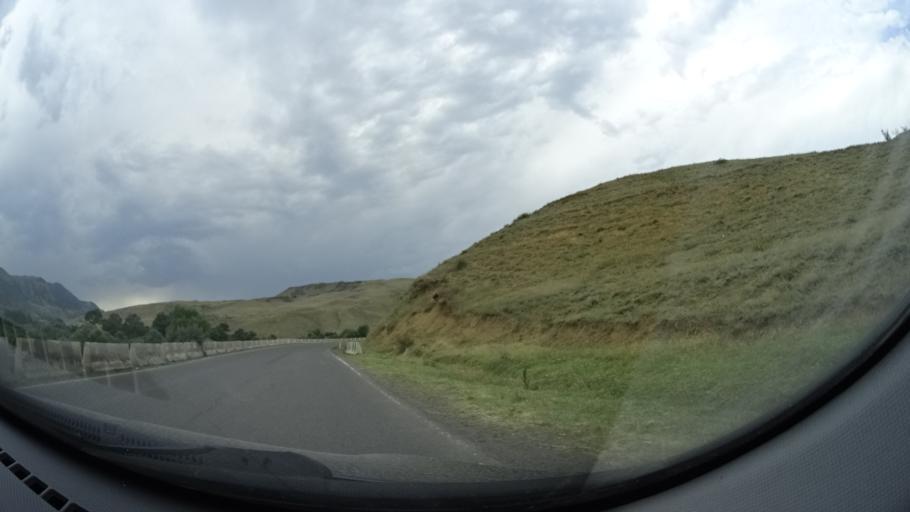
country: GE
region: Samtskhe-Javakheti
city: Aspindza
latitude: 41.5952
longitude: 43.1986
